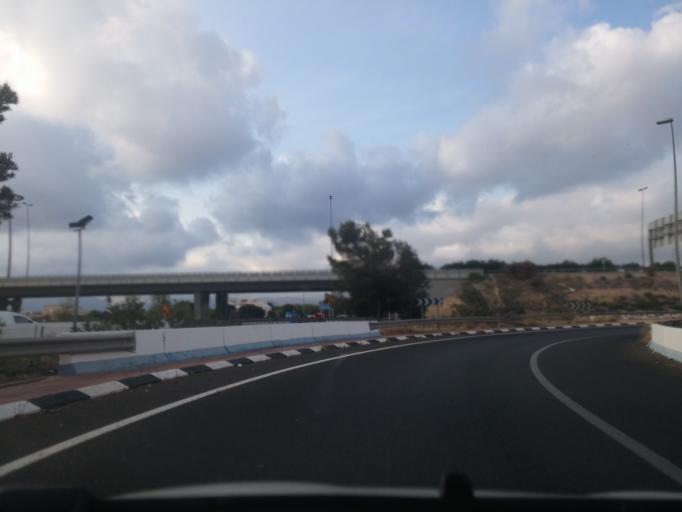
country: ES
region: Valencia
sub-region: Provincia de Alicante
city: San Vicent del Raspeig
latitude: 38.3791
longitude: -0.5127
